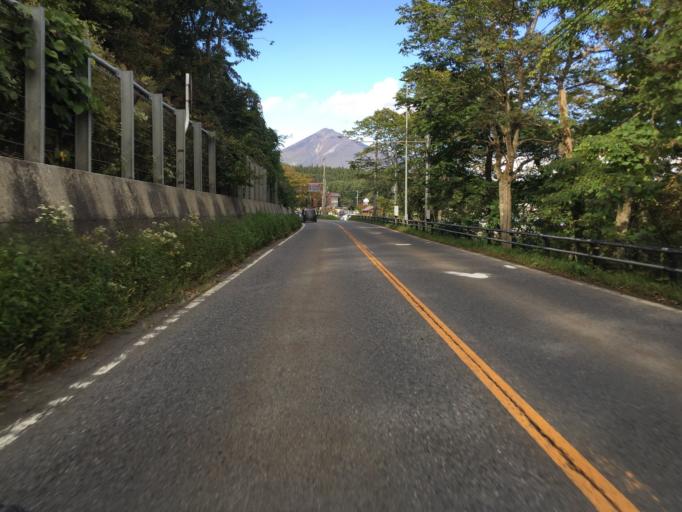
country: JP
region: Fukushima
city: Inawashiro
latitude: 37.5205
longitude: 140.0458
